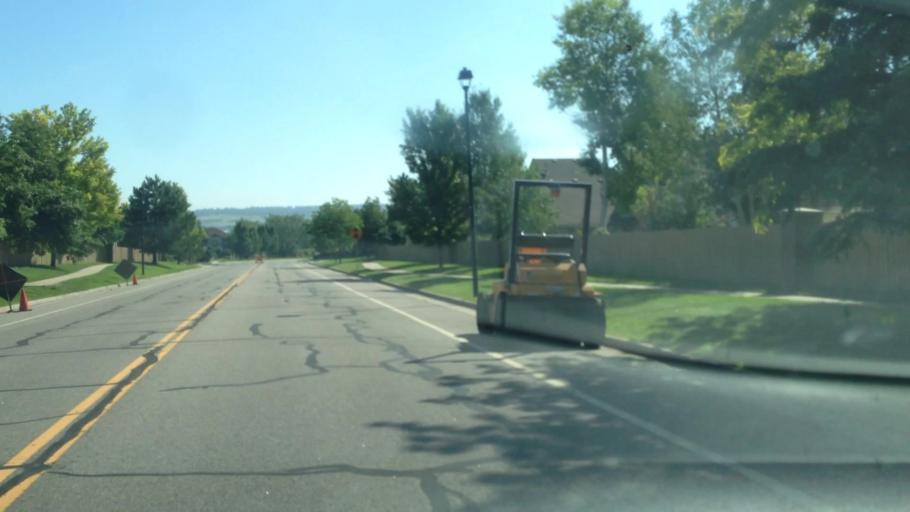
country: US
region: Colorado
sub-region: Douglas County
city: Stonegate
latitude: 39.5188
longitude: -104.7885
